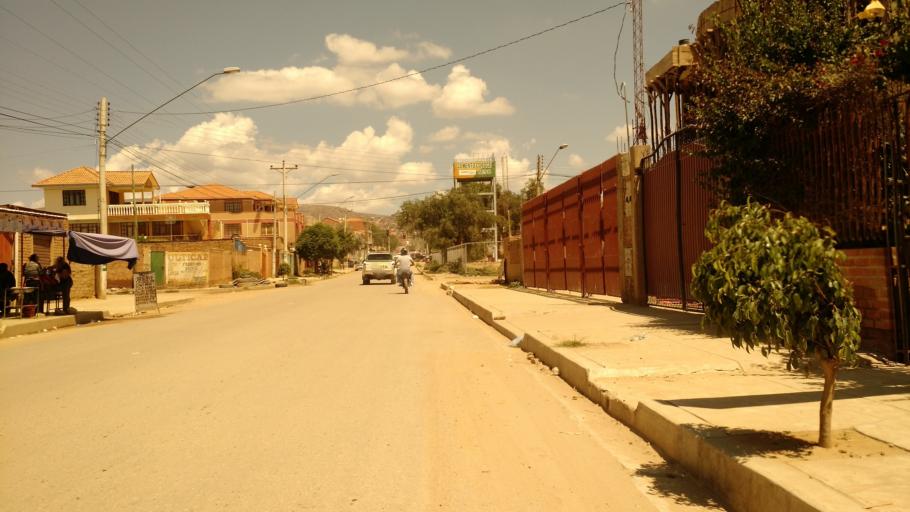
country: BO
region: Cochabamba
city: Cochabamba
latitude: -17.4455
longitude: -66.1554
